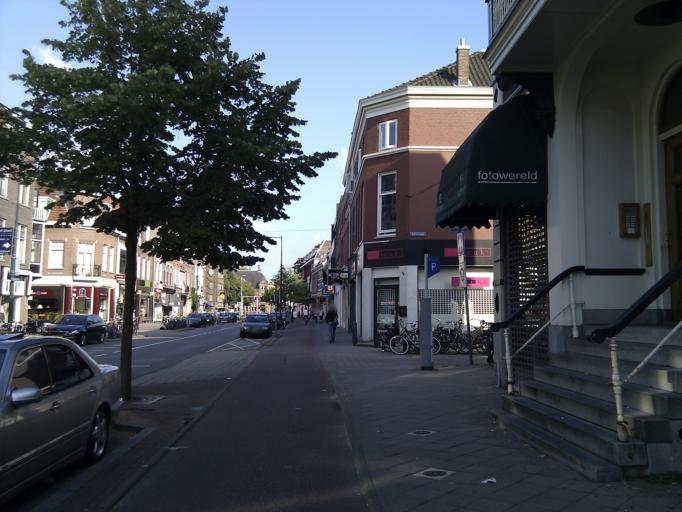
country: NL
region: Utrecht
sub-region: Gemeente Utrecht
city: Utrecht
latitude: 52.0921
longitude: 5.1303
